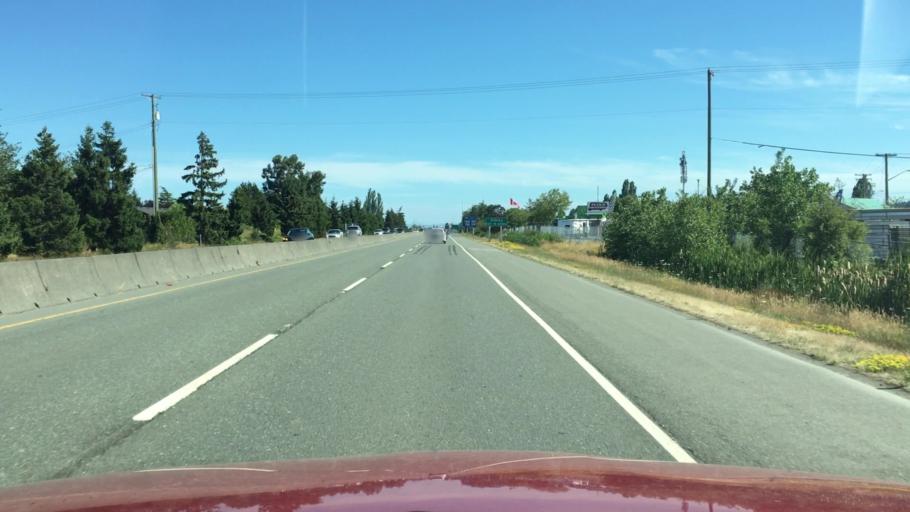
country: CA
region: British Columbia
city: North Saanich
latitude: 48.6560
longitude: -123.4123
